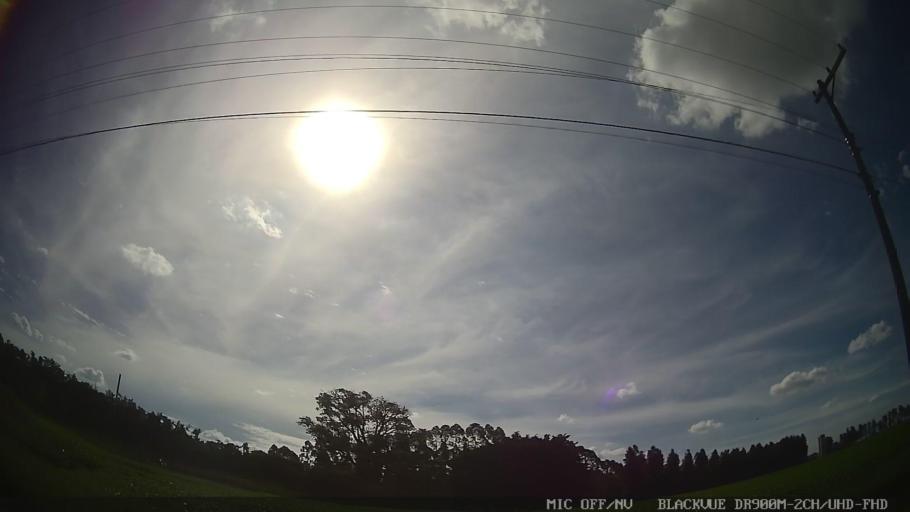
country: BR
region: Sao Paulo
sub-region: Artur Nogueira
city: Artur Nogueira
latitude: -22.6347
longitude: -47.0868
